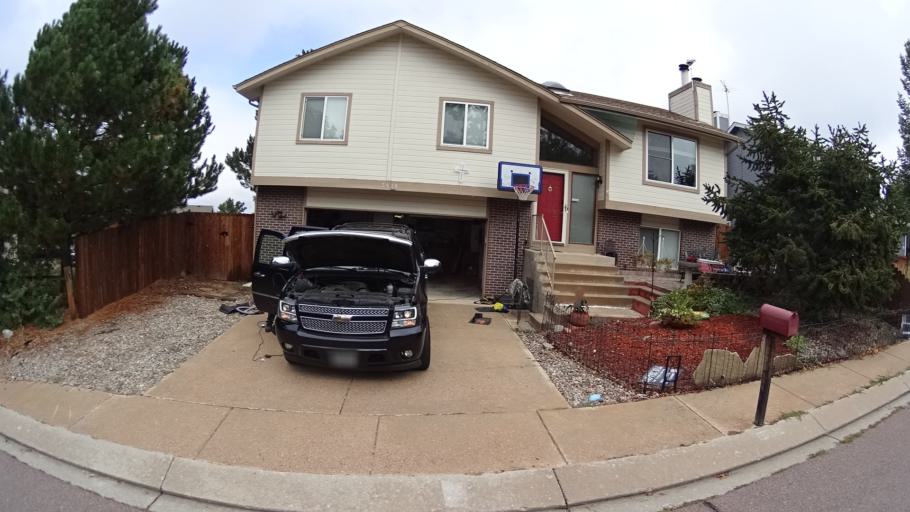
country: US
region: Colorado
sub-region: El Paso County
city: Cimarron Hills
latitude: 38.9242
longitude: -104.7643
